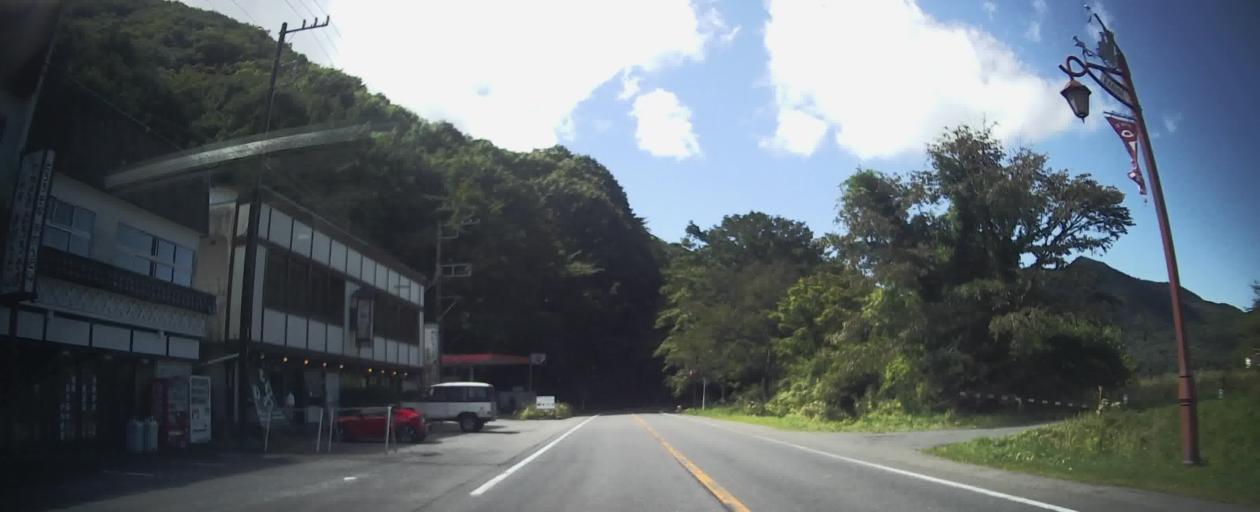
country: JP
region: Gunma
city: Nakanojomachi
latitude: 36.4679
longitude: 138.8722
